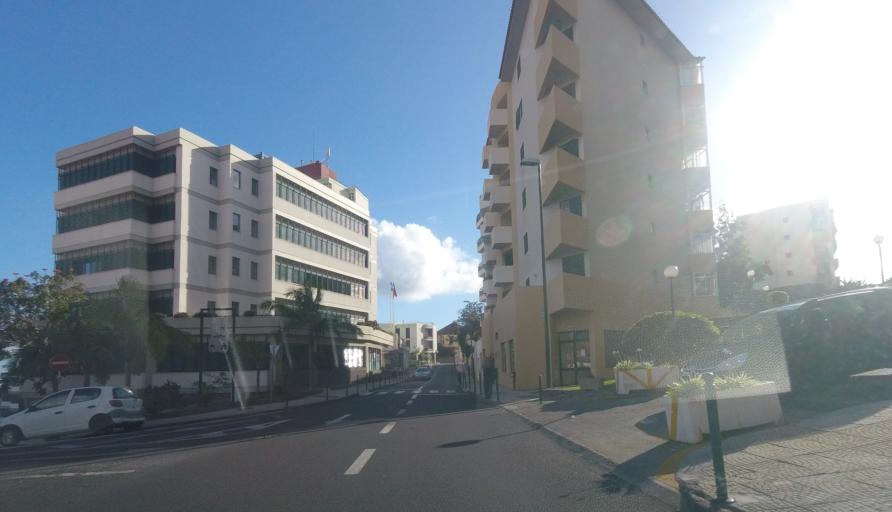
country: PT
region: Madeira
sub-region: Funchal
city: Nossa Senhora do Monte
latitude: 32.6530
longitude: -16.9061
